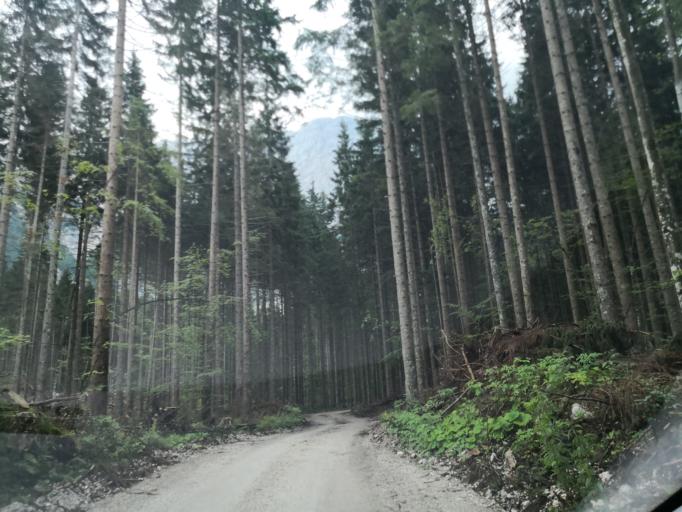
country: SI
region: Jezersko
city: Zgornje Jezersko
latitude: 46.3870
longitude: 14.5363
